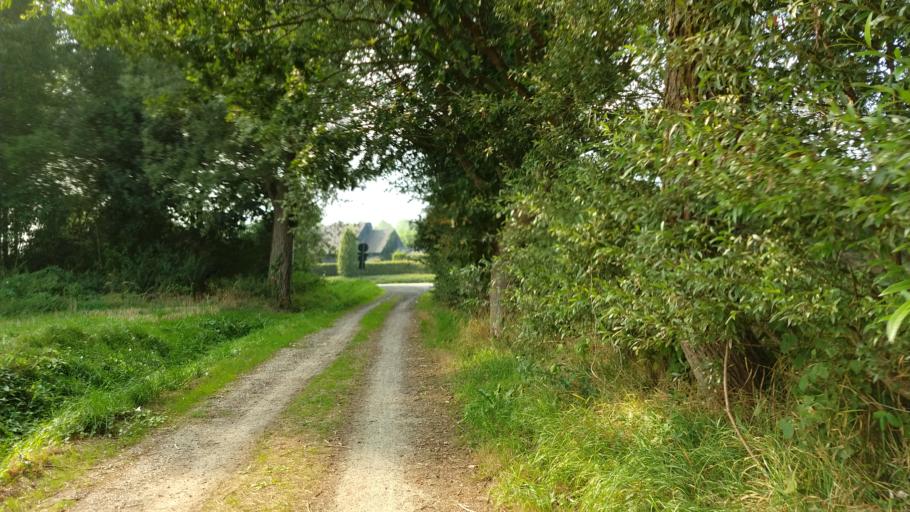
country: BE
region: Flanders
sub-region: Provincie Vlaams-Brabant
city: Rotselaar
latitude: 50.9570
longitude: 4.6902
